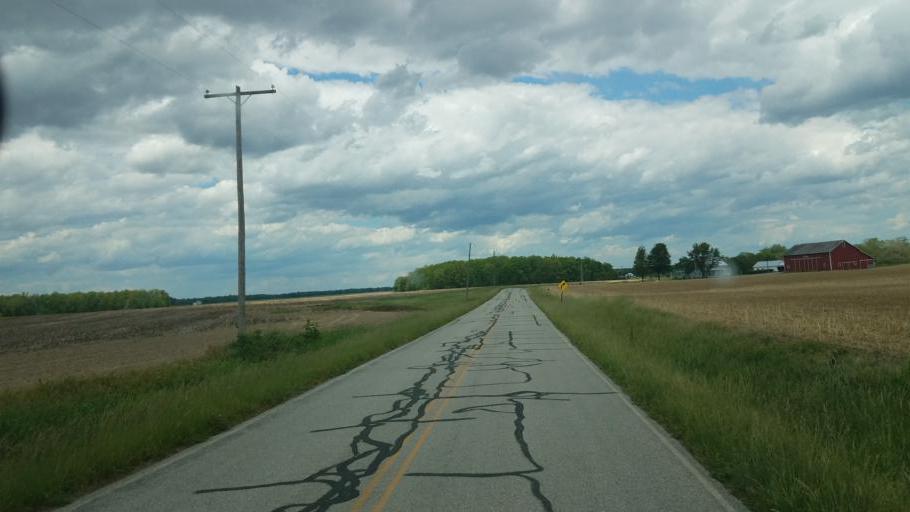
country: US
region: Ohio
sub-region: Huron County
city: Monroeville
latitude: 41.1652
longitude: -82.7738
